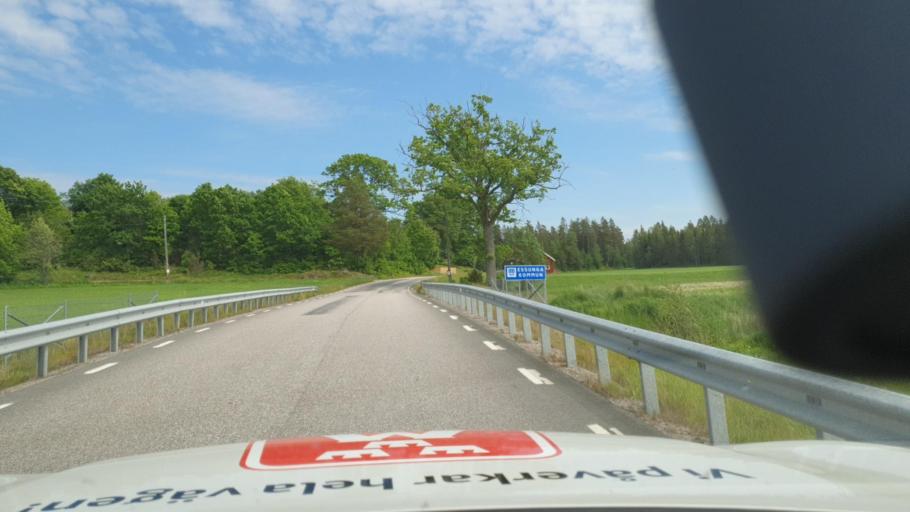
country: SE
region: Vaestra Goetaland
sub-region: Alingsas Kommun
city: Sollebrunn
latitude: 58.2127
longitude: 12.5339
